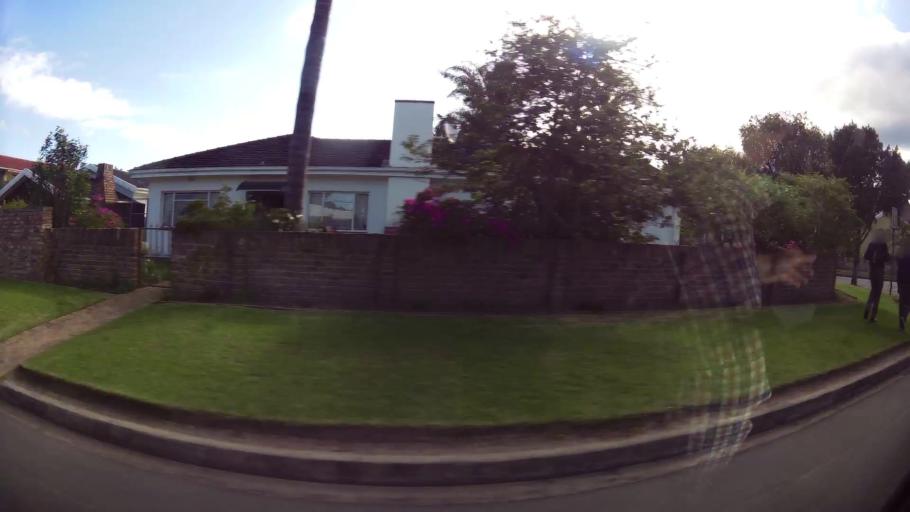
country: ZA
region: Western Cape
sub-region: Eden District Municipality
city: George
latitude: -33.9613
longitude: 22.4810
